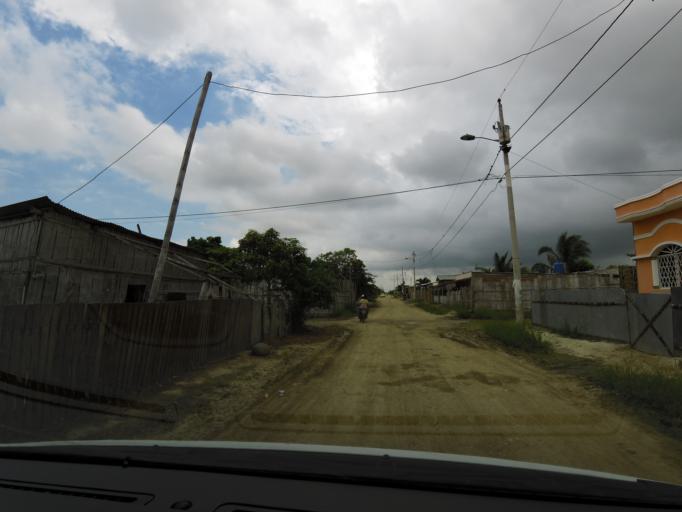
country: EC
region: El Oro
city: Huaquillas
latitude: -3.4851
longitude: -80.2052
